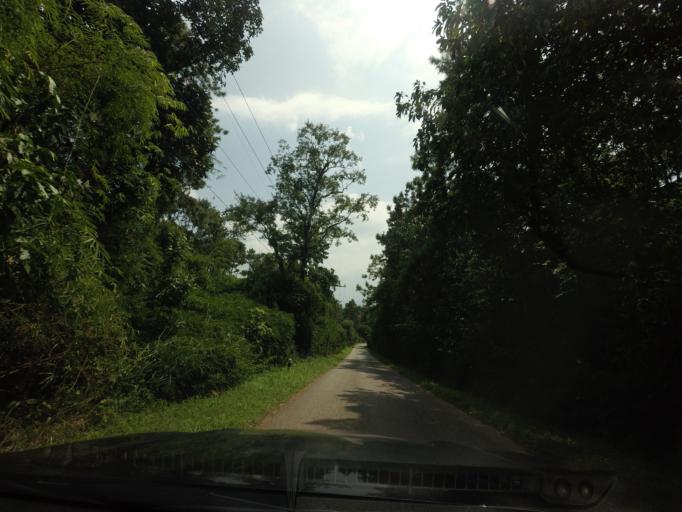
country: TH
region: Loei
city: Phu Ruea
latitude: 17.4694
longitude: 101.3551
